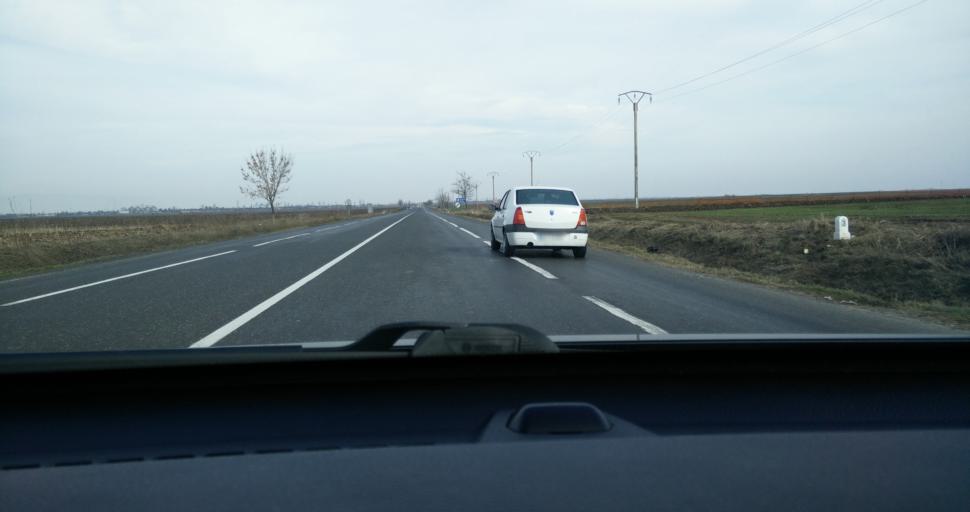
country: RO
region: Buzau
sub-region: Comuna Mihailesti
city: Mihailesti
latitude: 44.8938
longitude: 26.6873
